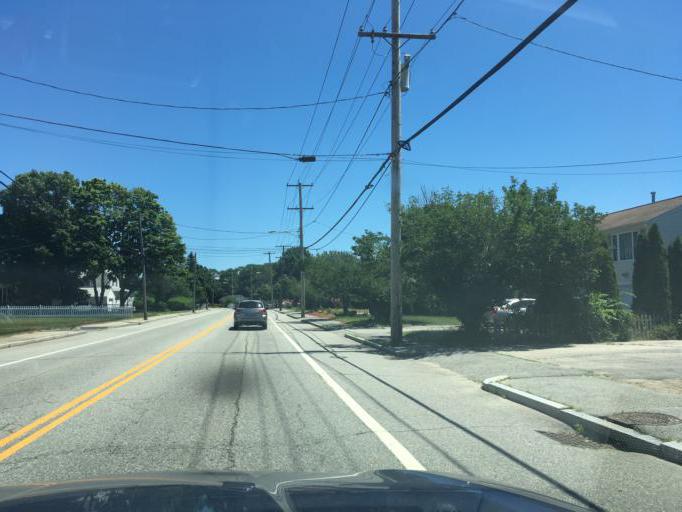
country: US
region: Rhode Island
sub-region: Kent County
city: Warwick
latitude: 41.7006
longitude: -71.3917
